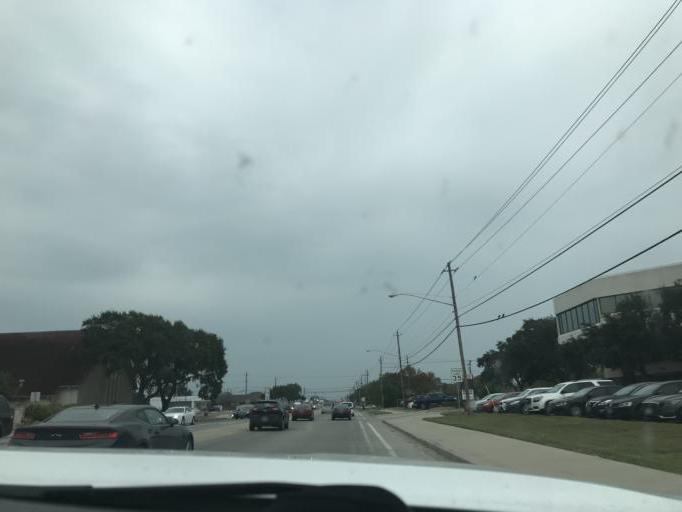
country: US
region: Texas
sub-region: Nueces County
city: Corpus Christi
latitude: 27.6984
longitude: -97.3757
